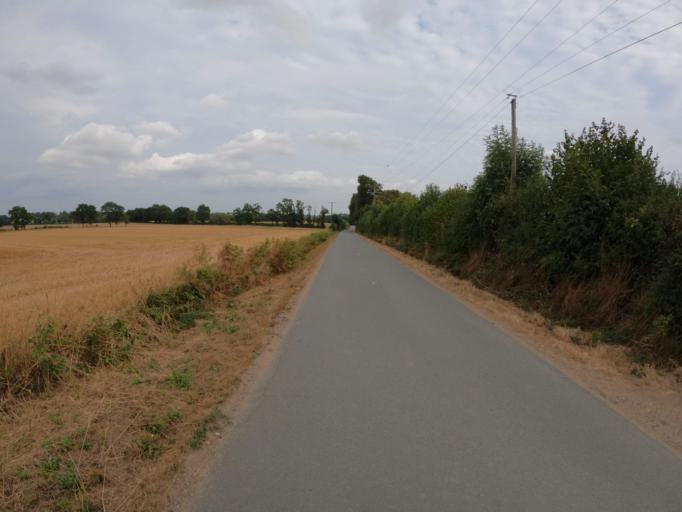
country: FR
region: Pays de la Loire
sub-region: Departement de Maine-et-Loire
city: La Romagne
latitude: 47.0508
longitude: -1.0029
